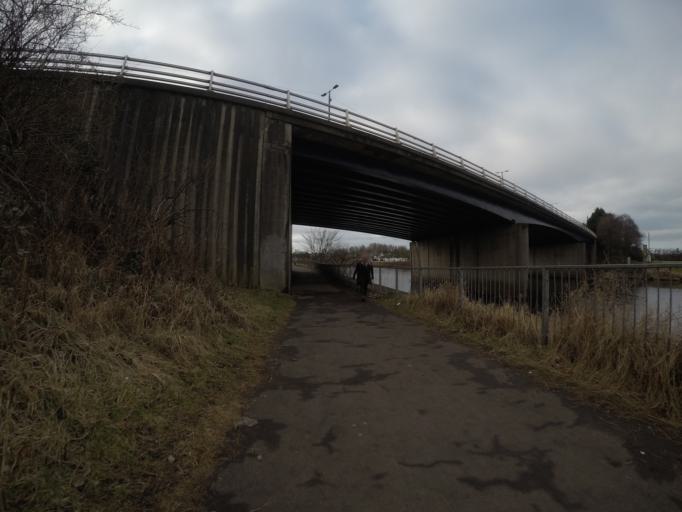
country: GB
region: Scotland
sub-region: North Ayrshire
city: Irvine
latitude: 55.6190
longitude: -4.6731
